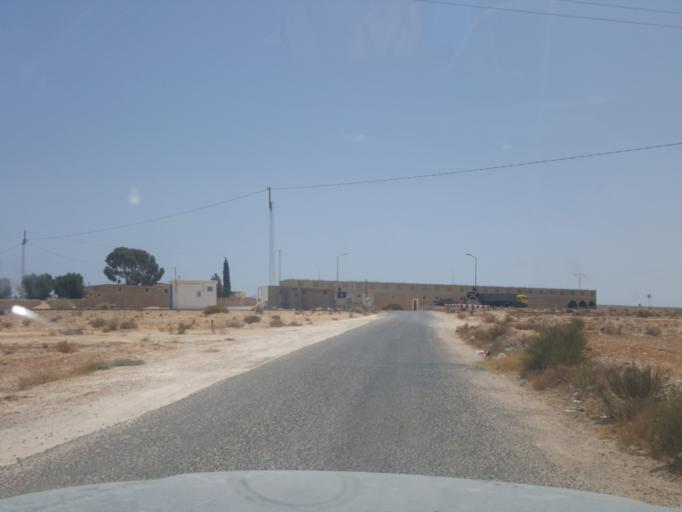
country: TN
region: Qabis
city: Gabes
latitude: 34.0545
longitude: 9.9844
